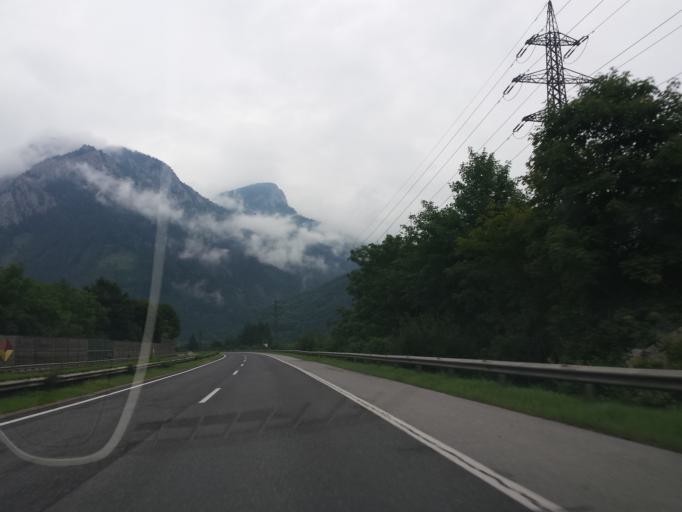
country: AT
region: Styria
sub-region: Politischer Bezirk Graz-Umgebung
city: Rothelstein
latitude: 47.3061
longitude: 15.3686
